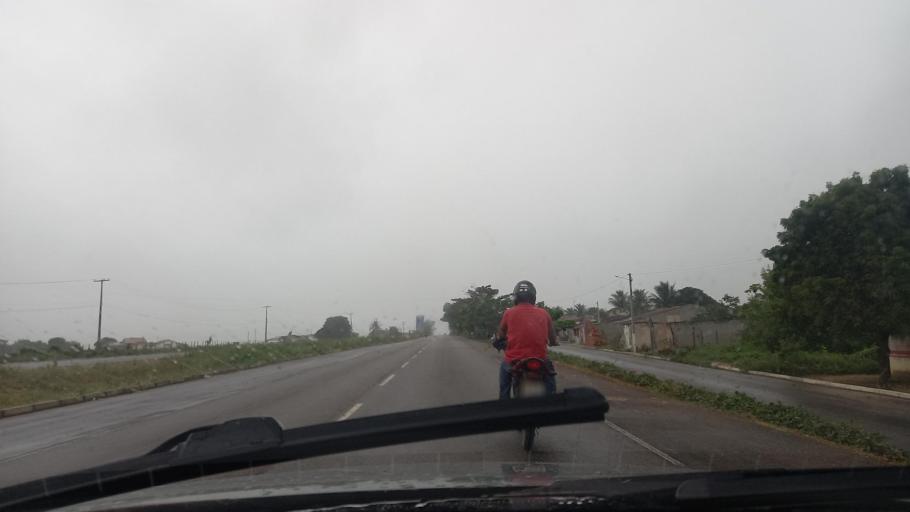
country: BR
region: Alagoas
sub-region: Lagoa Da Canoa
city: Lagoa da Canoa
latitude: -9.7000
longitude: -36.8001
